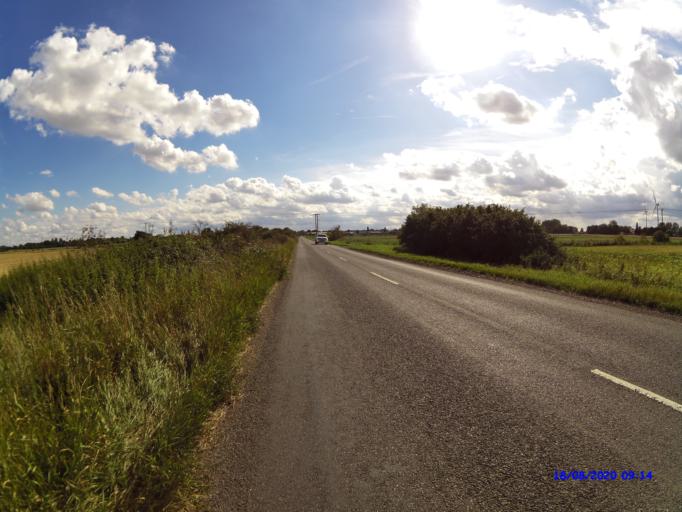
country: GB
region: England
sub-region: Cambridgeshire
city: Ramsey
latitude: 52.4620
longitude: -0.1026
